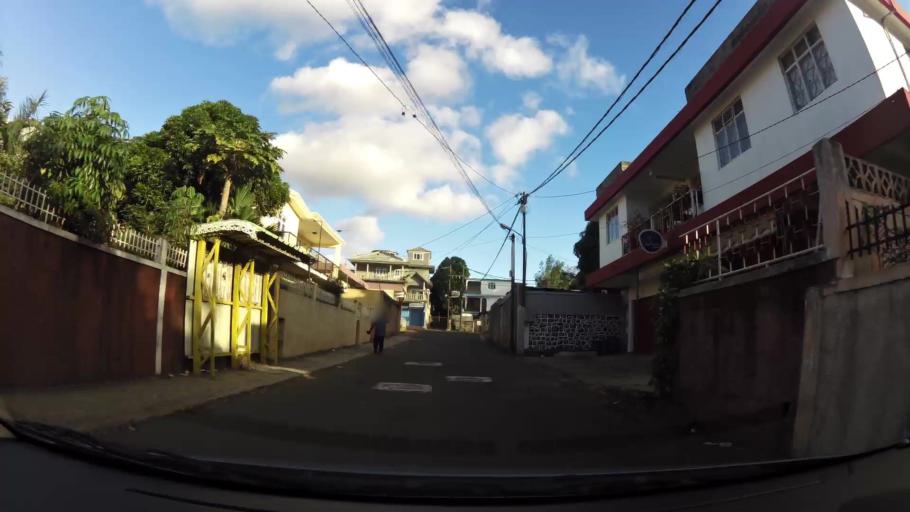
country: MU
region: Black River
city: Petite Riviere
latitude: -20.2208
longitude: 57.4641
